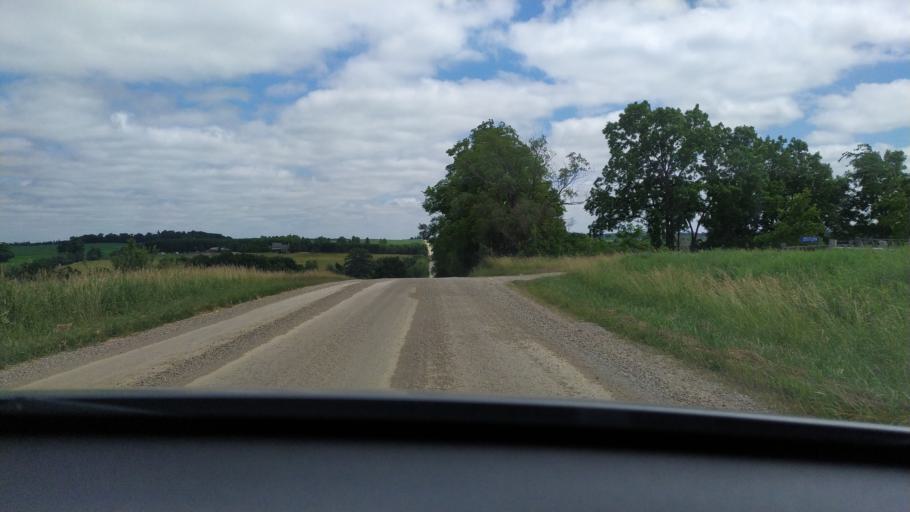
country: CA
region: Ontario
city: Stratford
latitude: 43.2734
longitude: -80.9773
